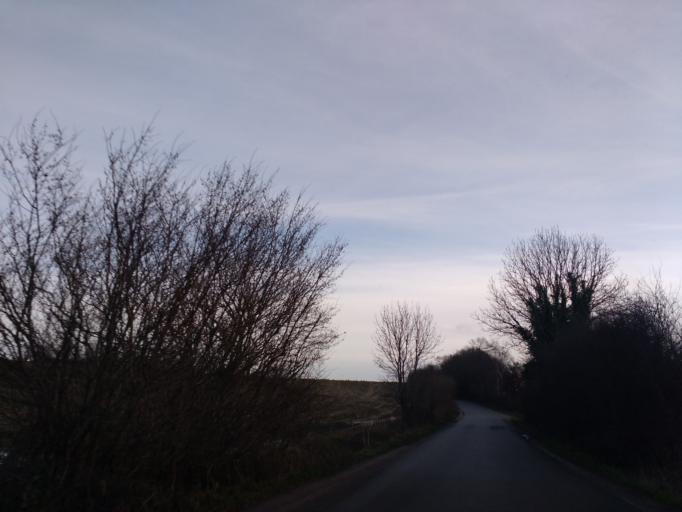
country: DE
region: Schleswig-Holstein
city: Heinkenborstel
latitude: 54.1324
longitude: 9.7595
